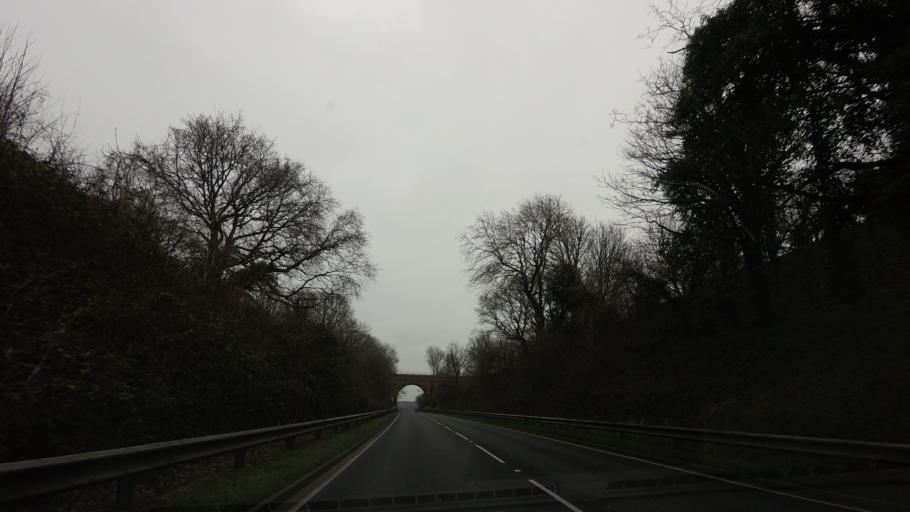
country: GB
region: England
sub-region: East Sussex
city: Bexhill-on-Sea
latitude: 50.8561
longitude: 0.4777
